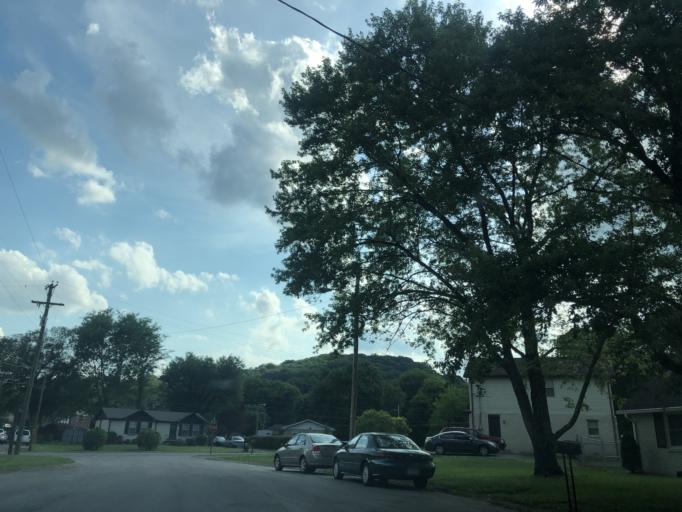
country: US
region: Tennessee
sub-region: Davidson County
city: Nashville
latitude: 36.2262
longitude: -86.8241
